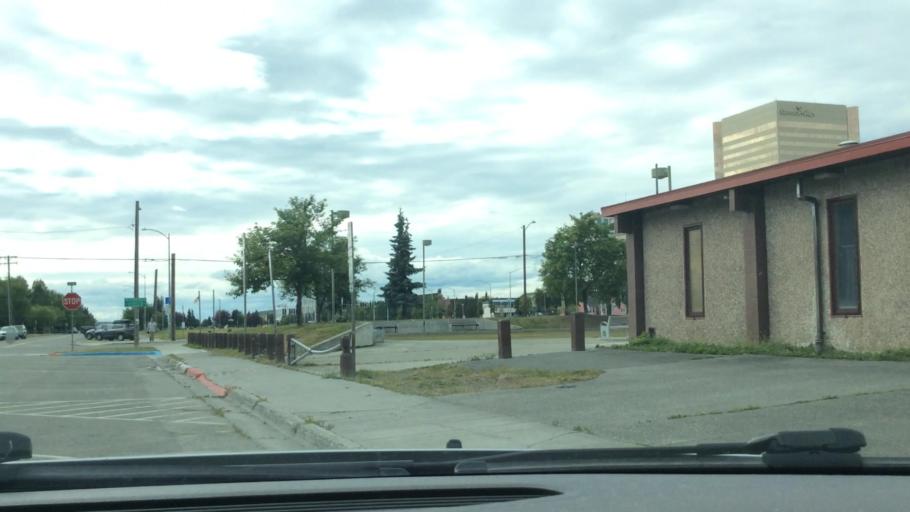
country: US
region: Alaska
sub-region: Anchorage Municipality
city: Anchorage
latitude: 61.2128
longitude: -149.8900
